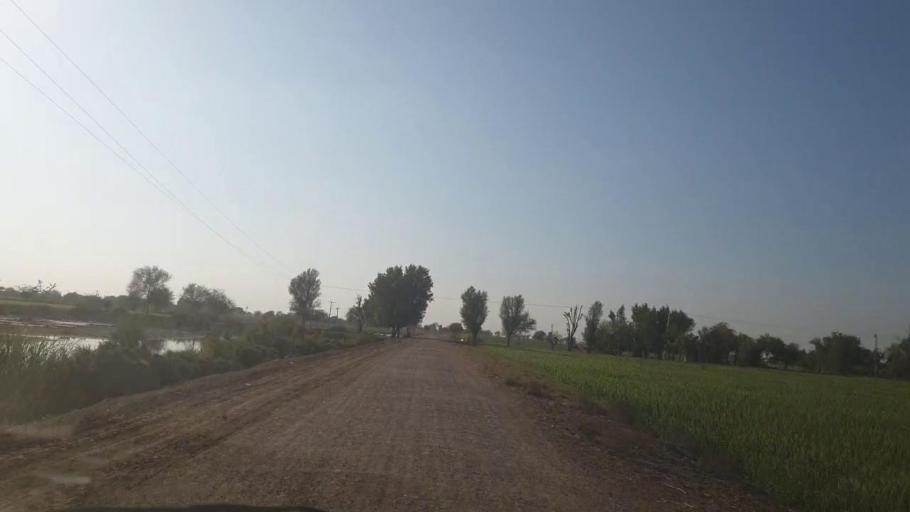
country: PK
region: Sindh
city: Mirwah Gorchani
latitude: 25.4295
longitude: 69.1274
